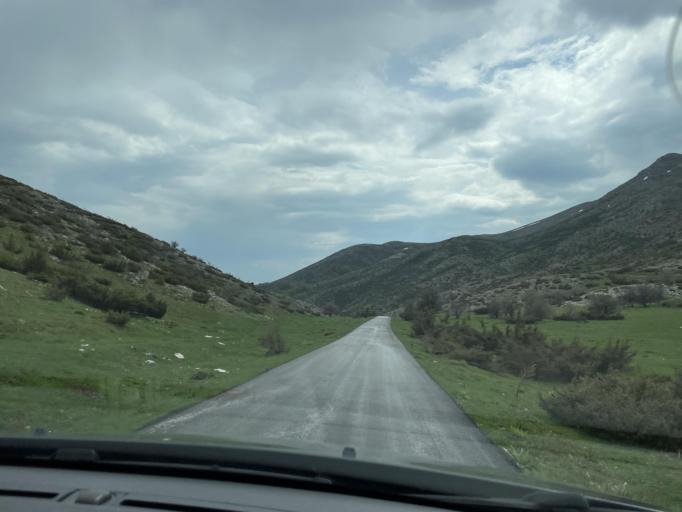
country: MK
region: Opstina Rostusa
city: Rostusha
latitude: 41.6188
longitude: 20.6850
